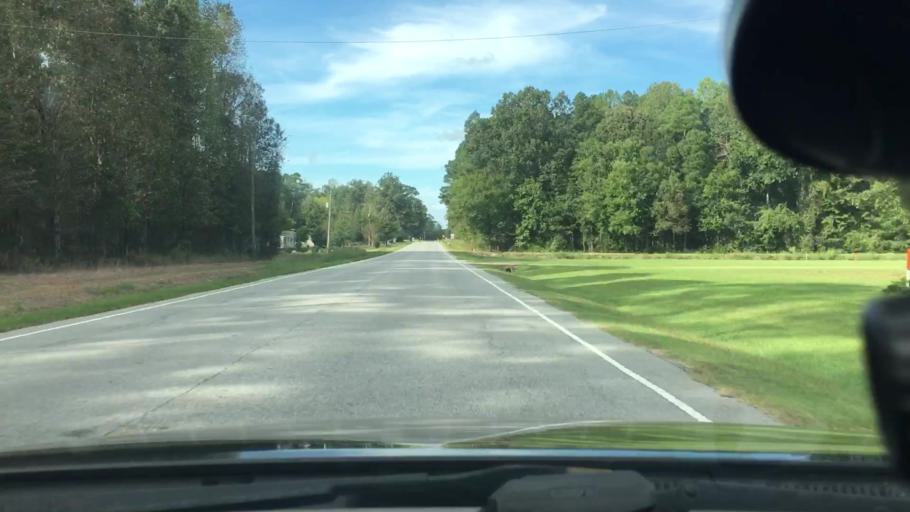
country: US
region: North Carolina
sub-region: Pitt County
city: Windsor
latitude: 35.4435
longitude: -77.2634
